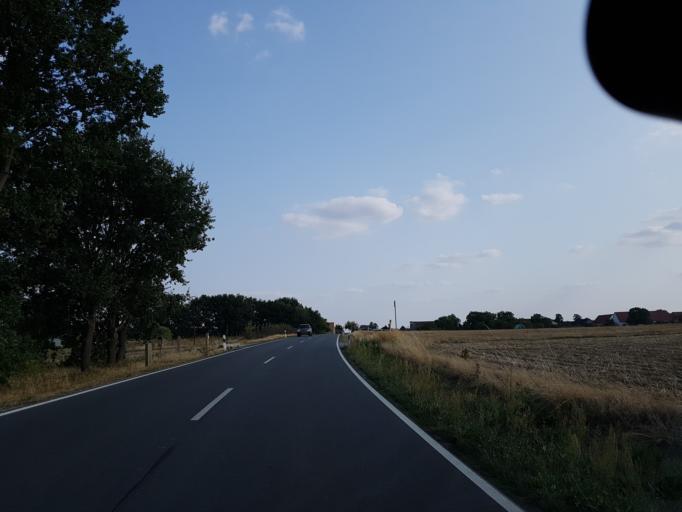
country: DE
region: Saxony
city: Dommitzsch
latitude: 51.6595
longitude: 12.8570
